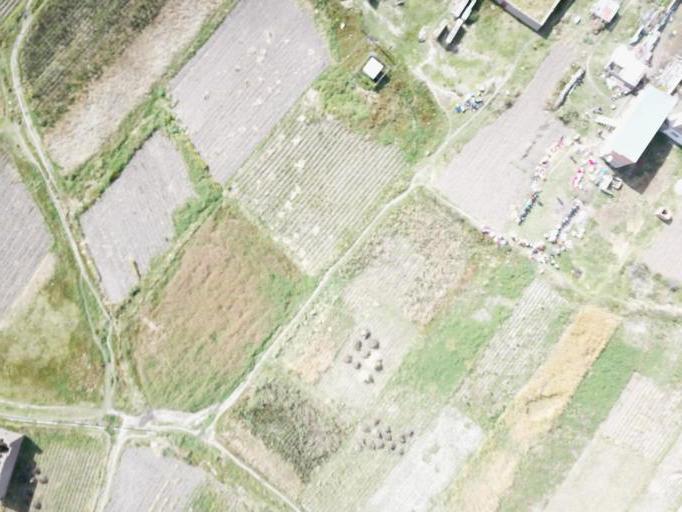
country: BO
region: La Paz
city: Achacachi
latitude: -16.0537
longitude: -68.8146
